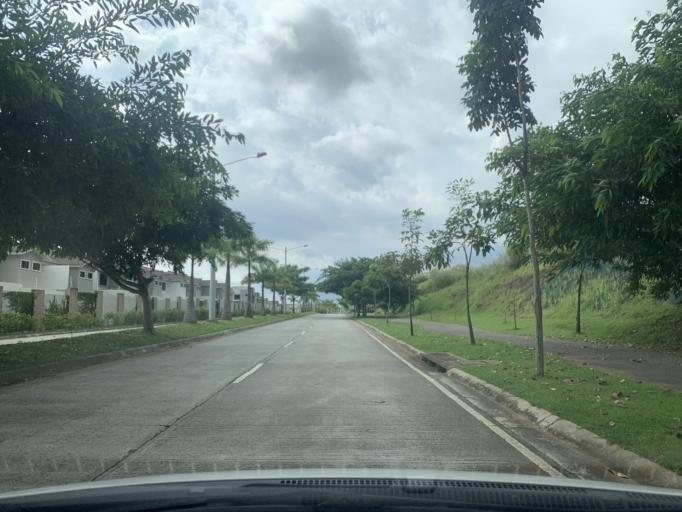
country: PA
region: Panama
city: San Miguelito
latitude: 9.0890
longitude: -79.4651
